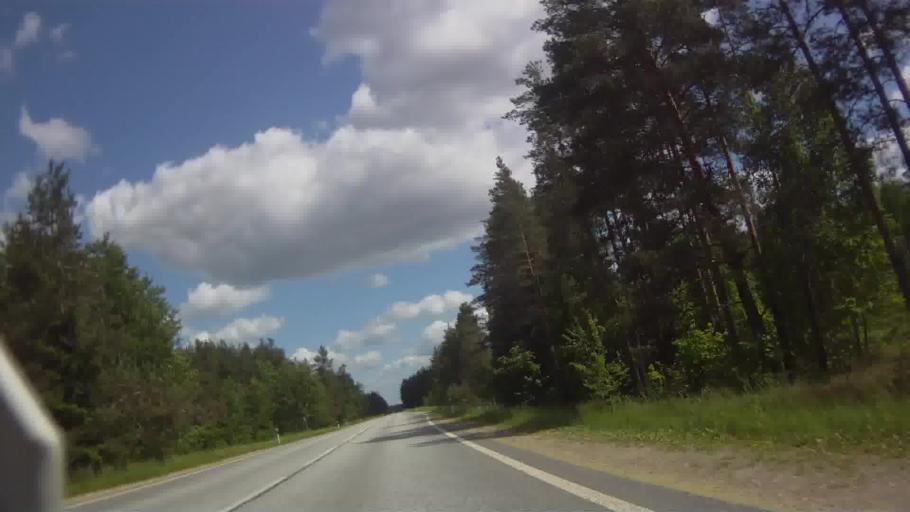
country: LV
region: Varaklani
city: Varaklani
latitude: 56.5579
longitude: 26.6071
